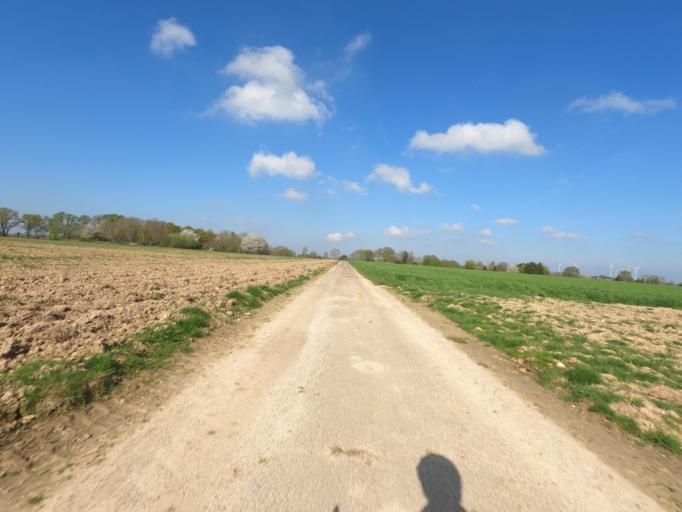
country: DE
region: North Rhine-Westphalia
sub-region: Regierungsbezirk Koln
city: Heinsberg
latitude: 51.0435
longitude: 6.0761
